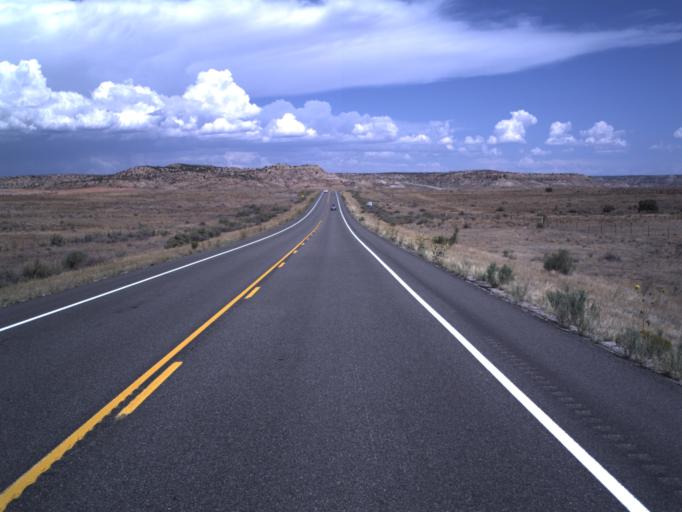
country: US
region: Utah
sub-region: San Juan County
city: Blanding
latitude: 37.4003
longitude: -109.4940
